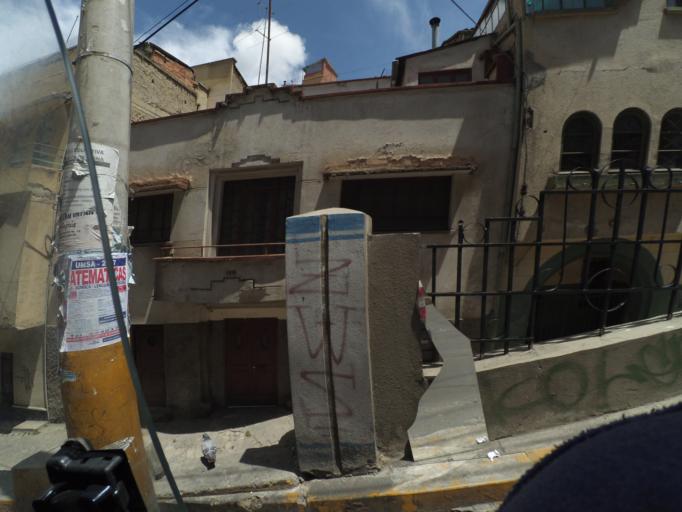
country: BO
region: La Paz
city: La Paz
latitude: -16.4943
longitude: -68.1302
